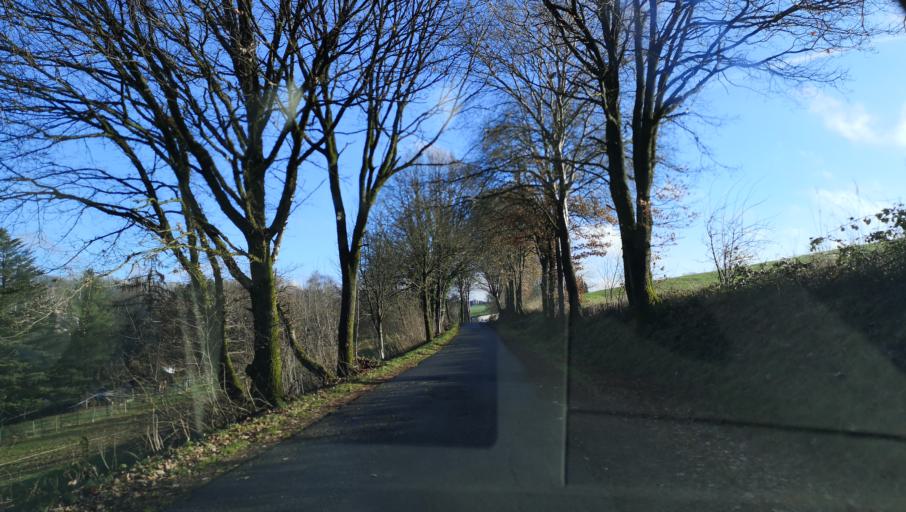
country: DE
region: North Rhine-Westphalia
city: Halver
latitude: 51.1853
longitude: 7.4300
